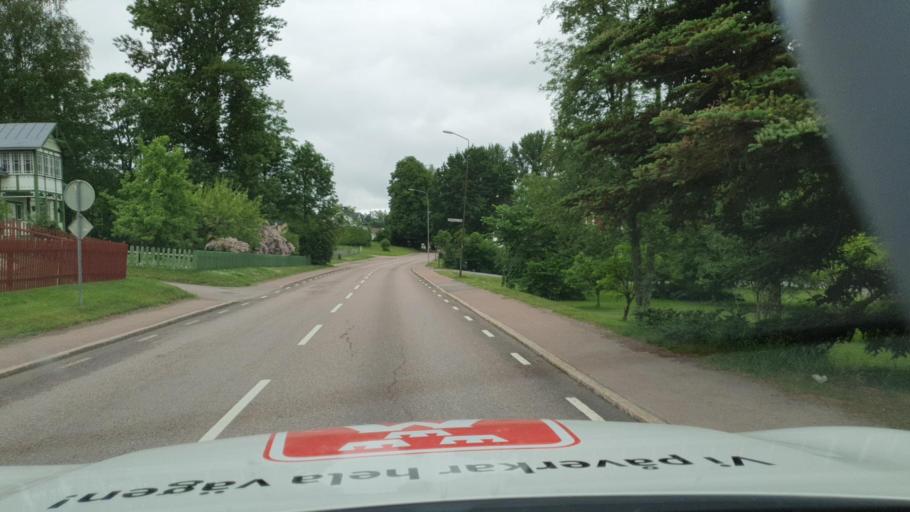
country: SE
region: Vaermland
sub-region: Karlstads Kommun
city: Edsvalla
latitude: 59.4336
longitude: 13.2116
